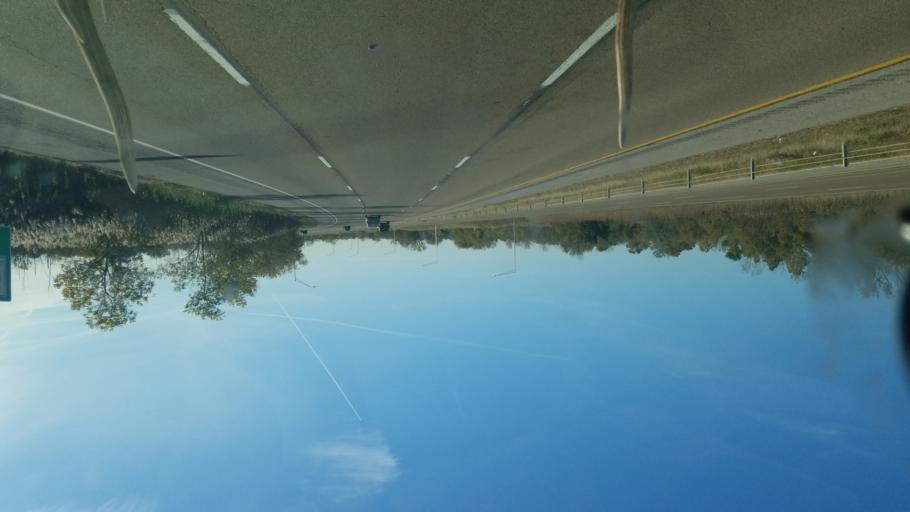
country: US
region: Illinois
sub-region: Saint Clair County
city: Fairmont City
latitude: 38.6621
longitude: -90.1019
